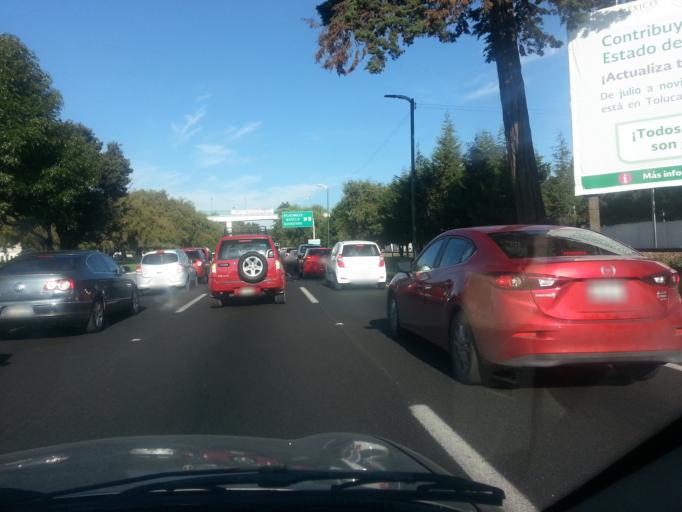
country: MX
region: Mexico
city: Santa Maria Totoltepec
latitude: 19.2880
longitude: -99.6164
